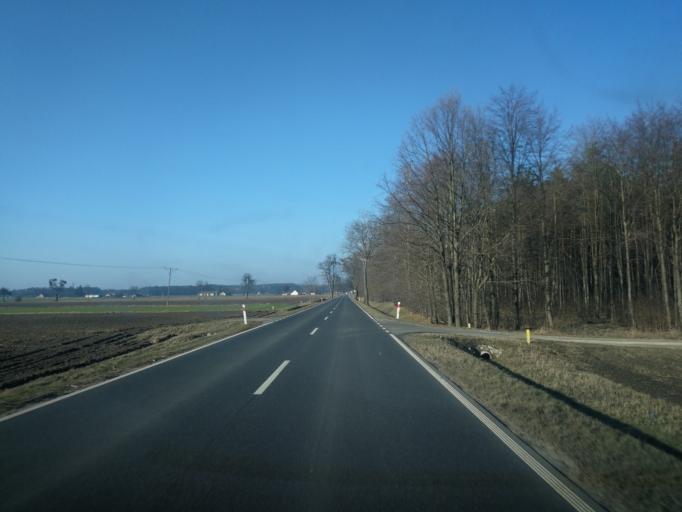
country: PL
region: Warmian-Masurian Voivodeship
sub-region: Powiat dzialdowski
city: Lidzbark
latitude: 53.3602
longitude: 19.8199
